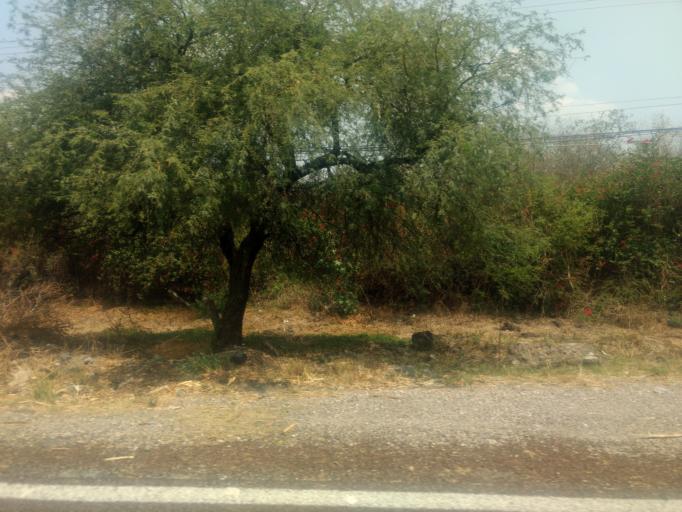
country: MX
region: Morelos
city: Puente de Ixtla
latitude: 18.6380
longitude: -99.3119
